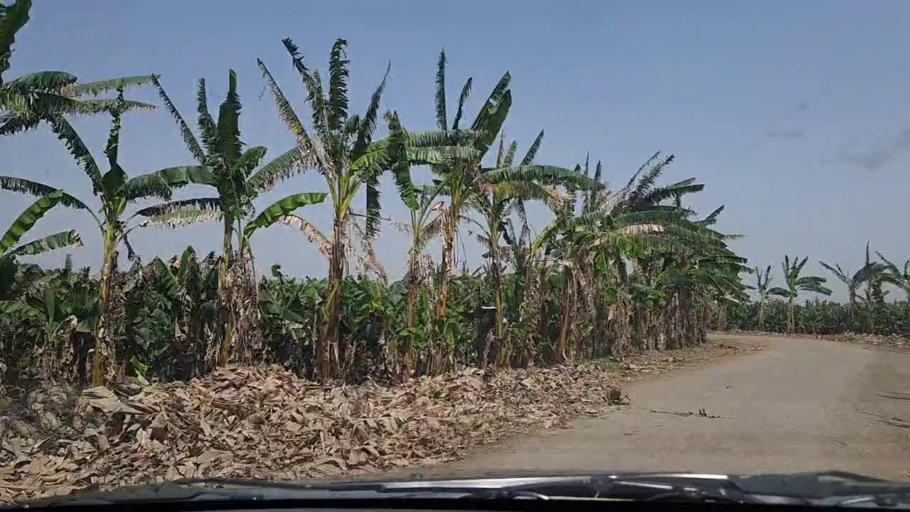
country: PK
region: Sindh
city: Keti Bandar
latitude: 24.2799
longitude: 67.6714
